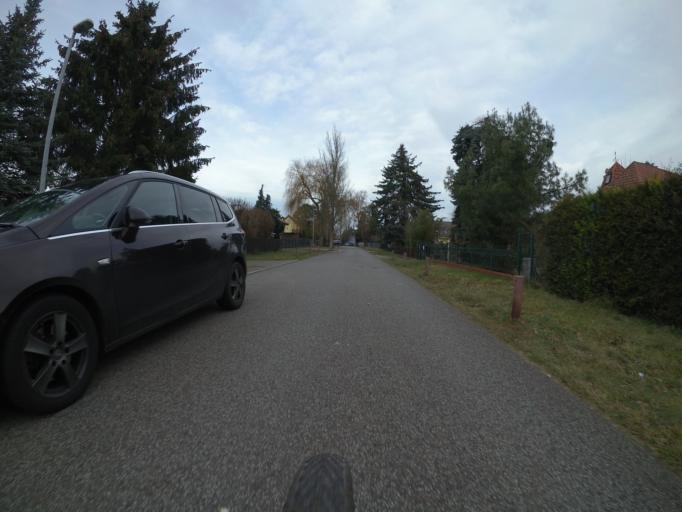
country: DE
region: Brandenburg
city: Schoneiche
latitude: 52.4703
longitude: 13.7263
